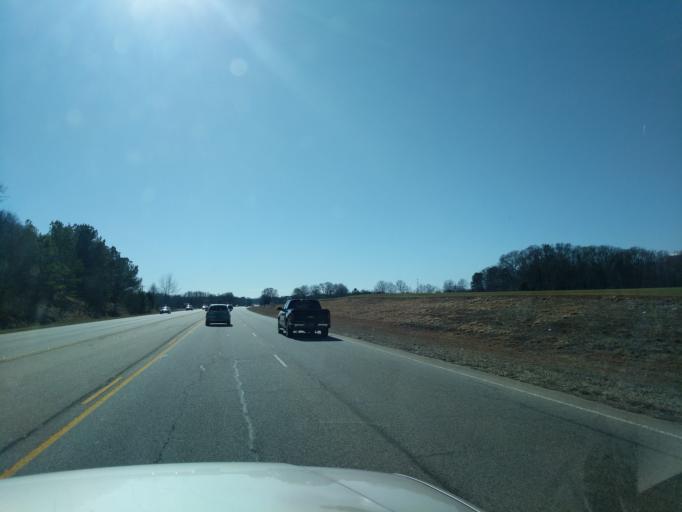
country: US
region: South Carolina
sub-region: Anderson County
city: Northlake
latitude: 34.6233
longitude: -82.6054
